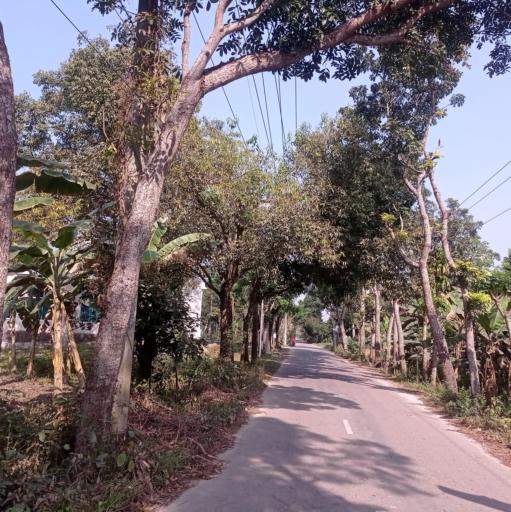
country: BD
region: Dhaka
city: Narsingdi
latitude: 24.0303
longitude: 90.6730
